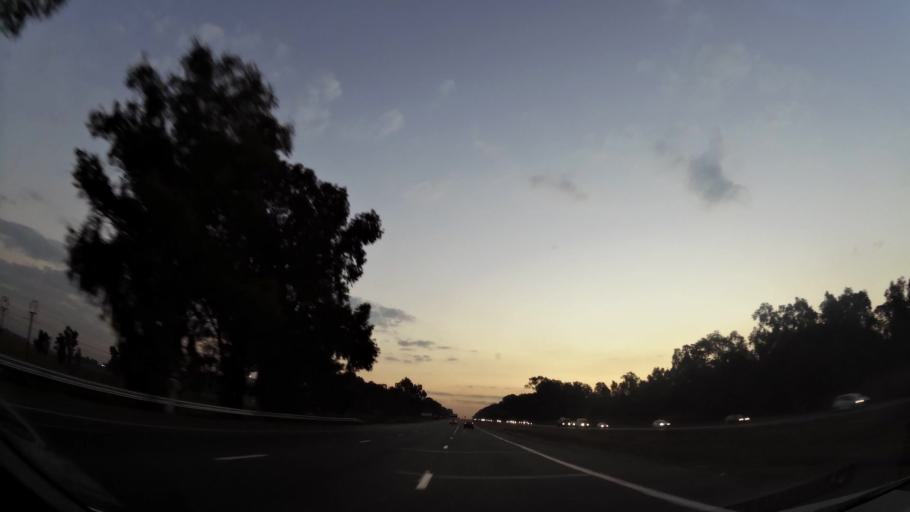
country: ZA
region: Gauteng
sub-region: Ekurhuleni Metropolitan Municipality
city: Boksburg
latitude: -26.2515
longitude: 28.2295
